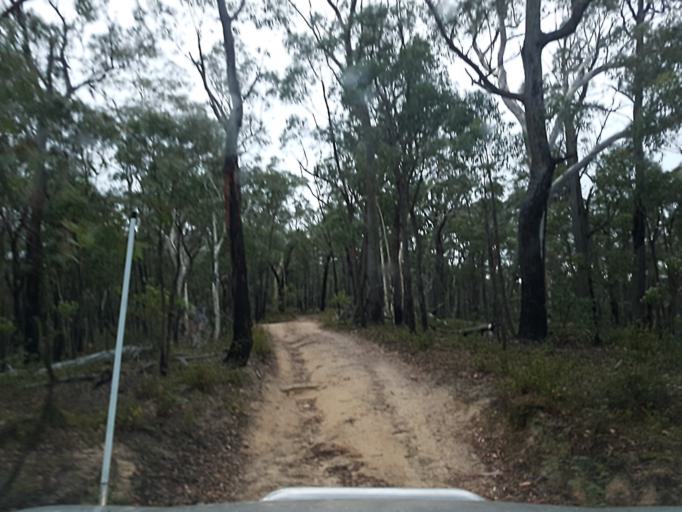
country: AU
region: New South Wales
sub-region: Snowy River
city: Jindabyne
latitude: -36.8524
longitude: 148.2282
